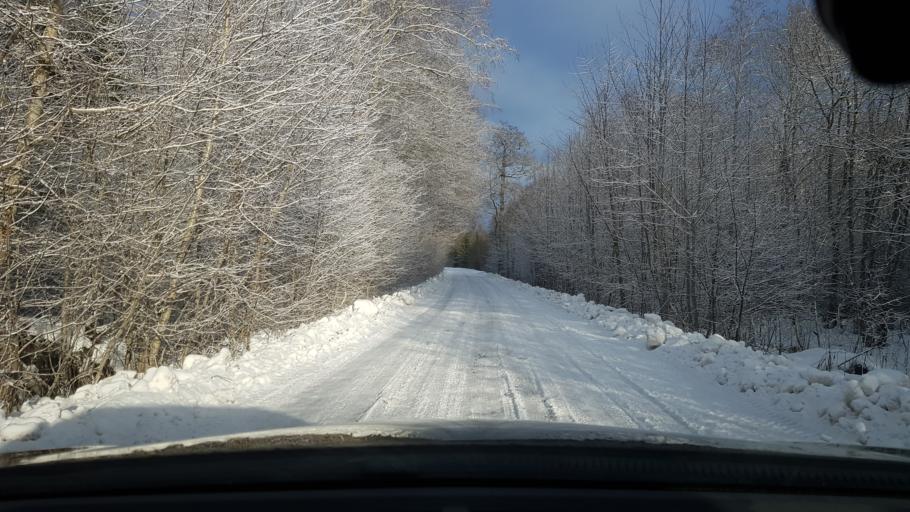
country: EE
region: Harju
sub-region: Keila linn
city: Keila
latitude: 59.3152
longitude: 24.2469
